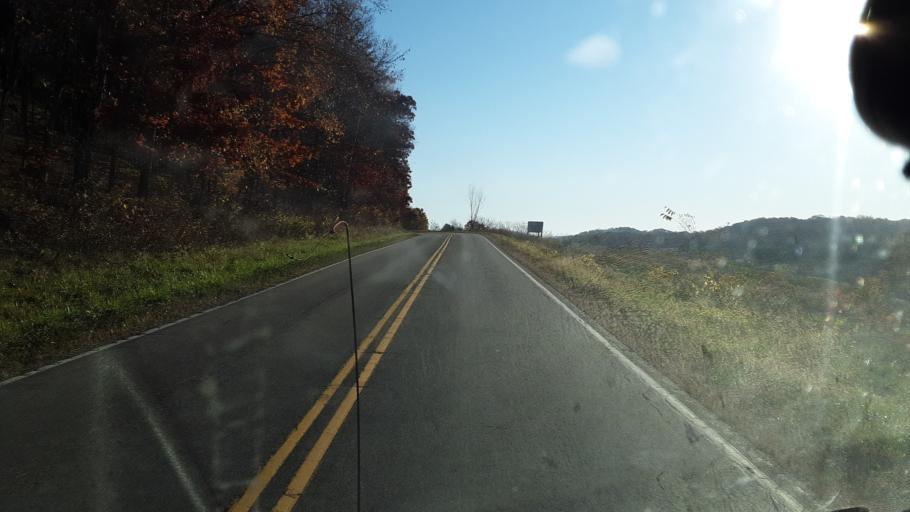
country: US
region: Wisconsin
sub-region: Vernon County
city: Hillsboro
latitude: 43.6602
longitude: -90.4244
